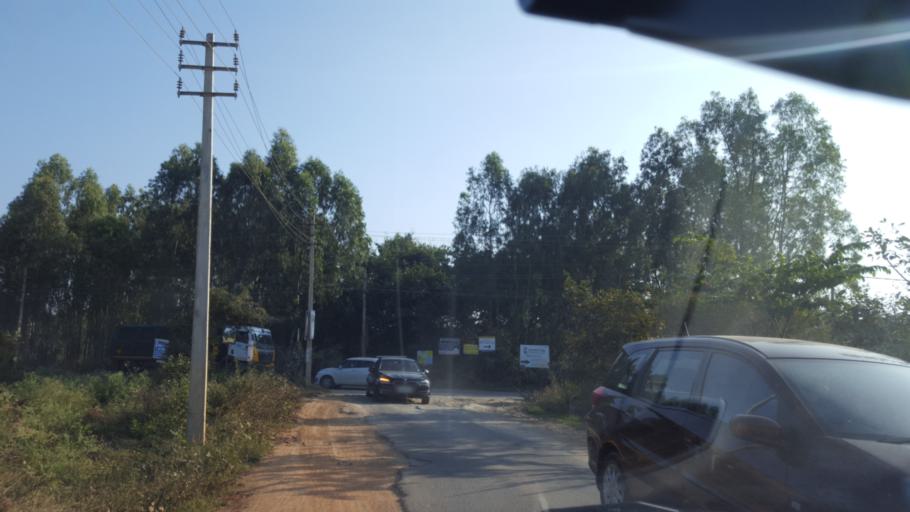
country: IN
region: Karnataka
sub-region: Bangalore Rural
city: Hoskote
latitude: 12.9185
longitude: 77.7572
